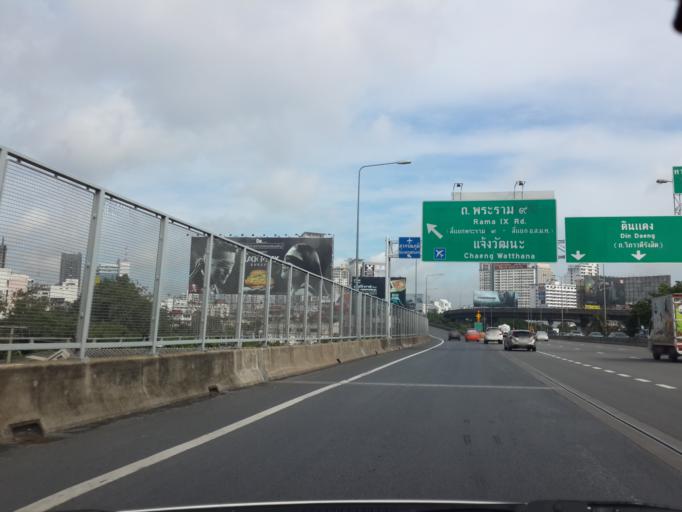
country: TH
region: Bangkok
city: Ratchathewi
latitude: 13.7552
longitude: 100.5455
